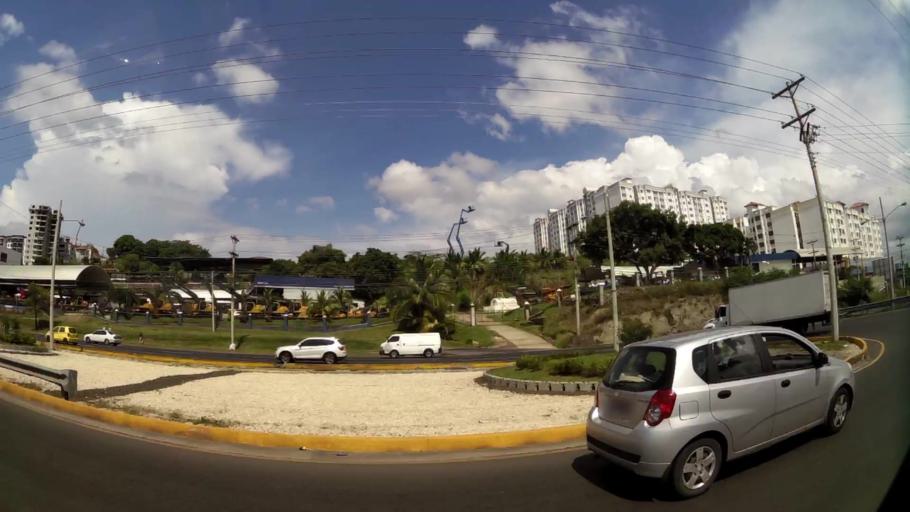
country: PA
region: Panama
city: San Miguelito
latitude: 9.0459
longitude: -79.4670
